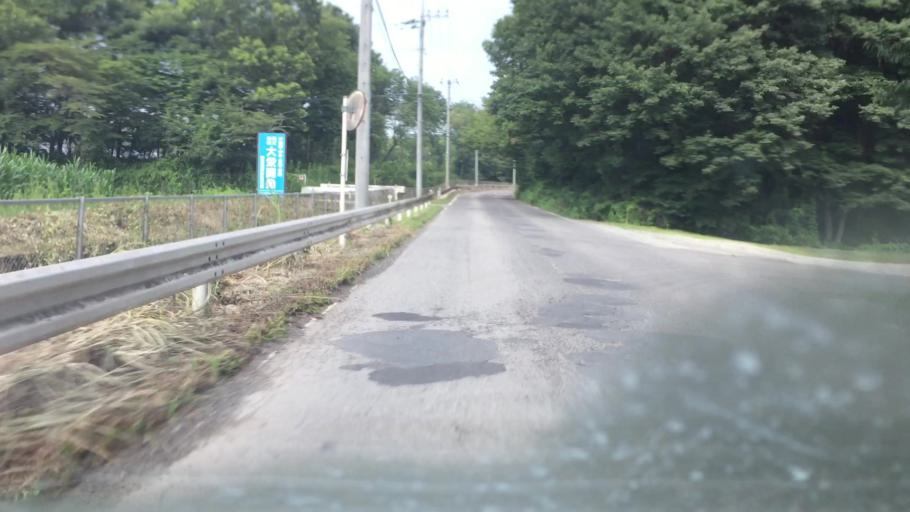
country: JP
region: Tochigi
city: Kuroiso
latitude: 36.9779
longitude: 139.9758
